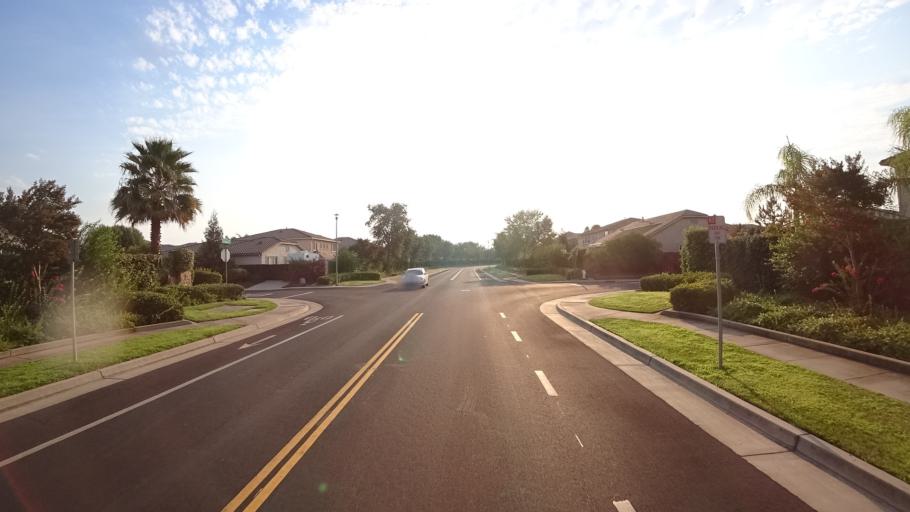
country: US
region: California
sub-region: Sacramento County
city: Laguna
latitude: 38.3829
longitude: -121.4475
